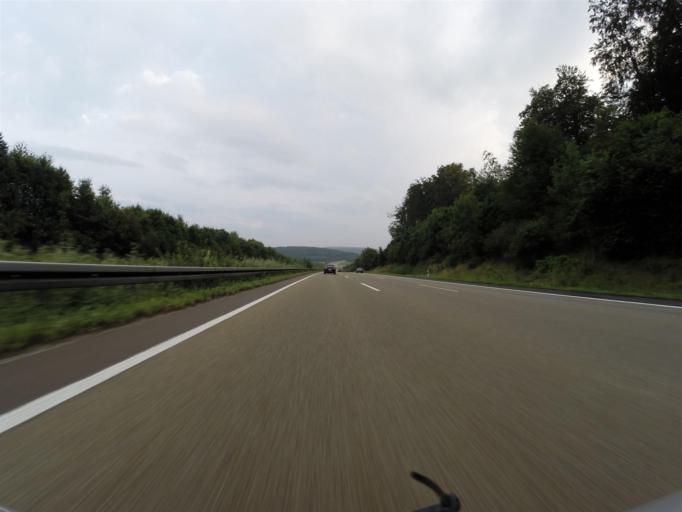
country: DE
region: Hesse
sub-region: Regierungsbezirk Kassel
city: Malsfeld
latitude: 51.0600
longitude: 9.4948
